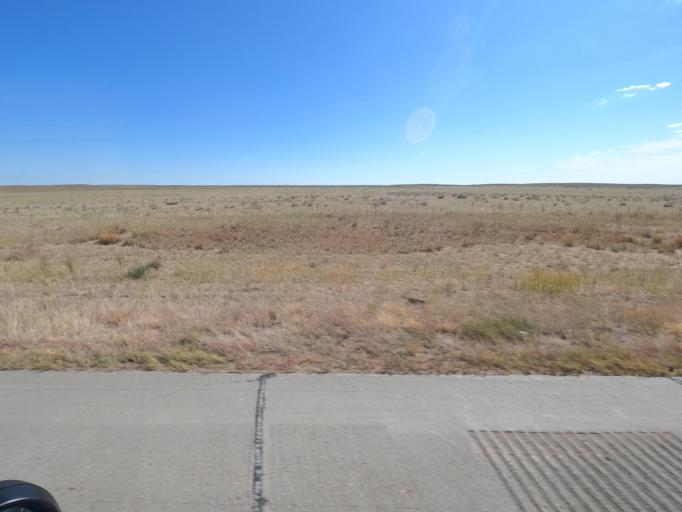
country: US
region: Colorado
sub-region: Weld County
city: Keenesburg
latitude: 40.2036
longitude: -104.2497
